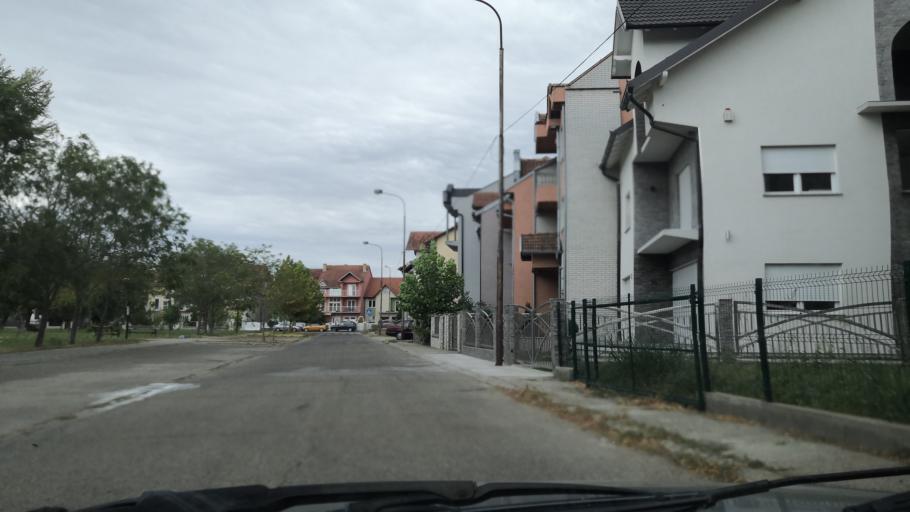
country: RS
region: Central Serbia
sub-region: Borski Okrug
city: Negotin
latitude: 44.2285
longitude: 22.5226
